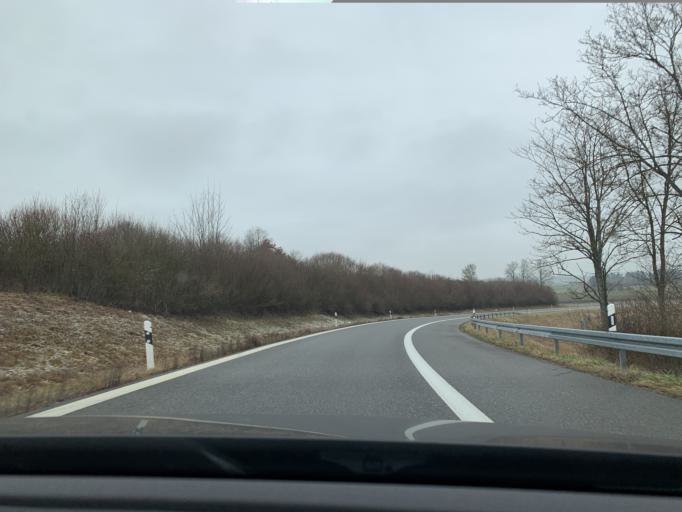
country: DE
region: Baden-Wuerttemberg
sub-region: Freiburg Region
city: Bad Durrheim
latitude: 47.9928
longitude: 8.5310
